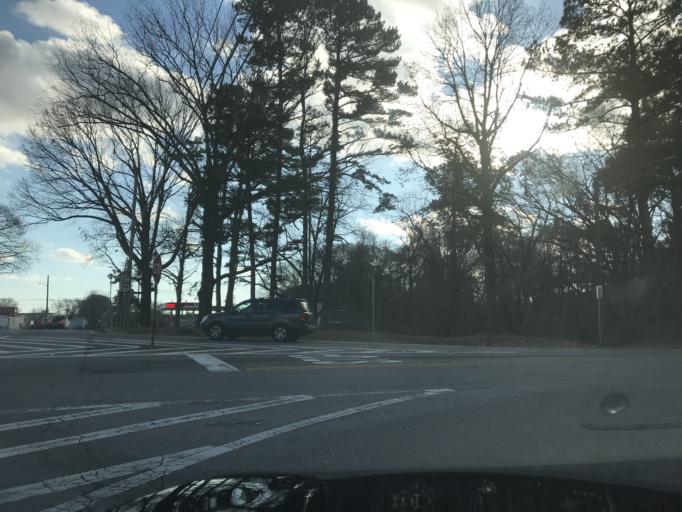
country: US
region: Georgia
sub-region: Fulton County
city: College Park
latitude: 33.6295
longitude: -84.4727
